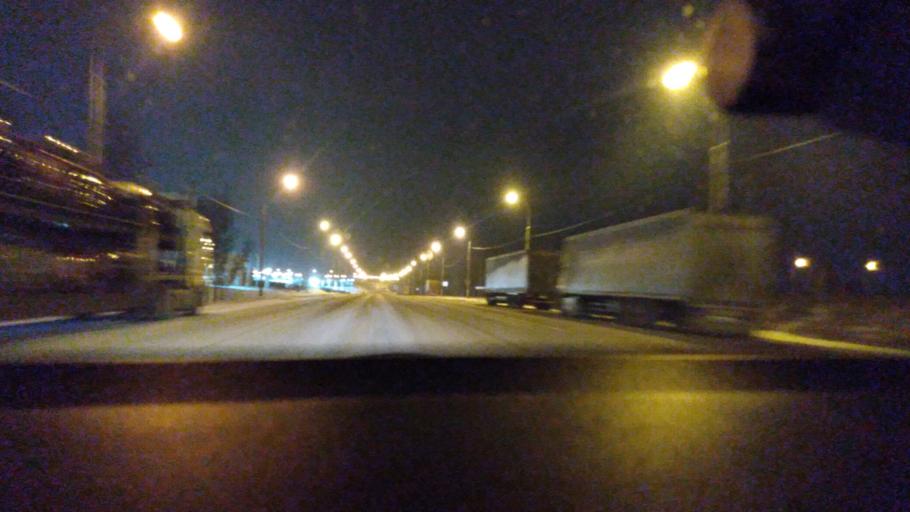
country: RU
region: Moskovskaya
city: Raduzhnyy
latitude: 55.1602
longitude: 38.6858
